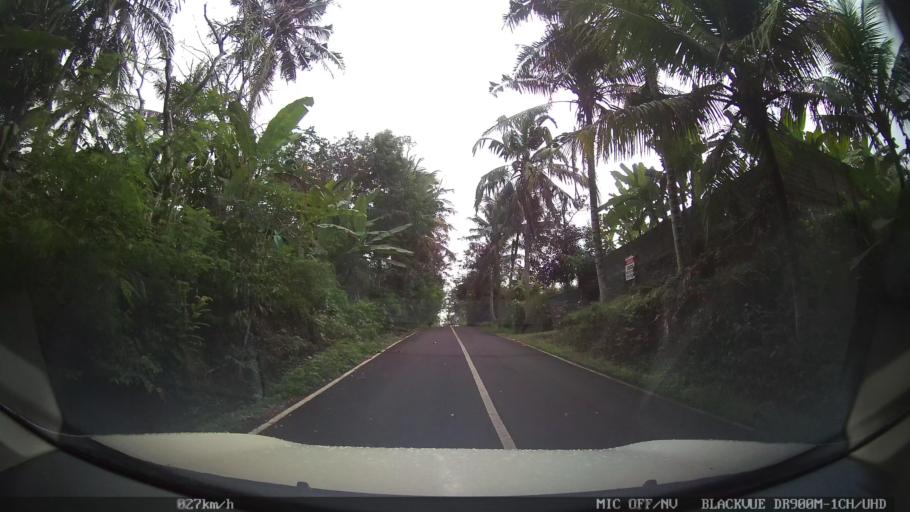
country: ID
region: Bali
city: Banjar Serangan
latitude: -8.5393
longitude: 115.1842
